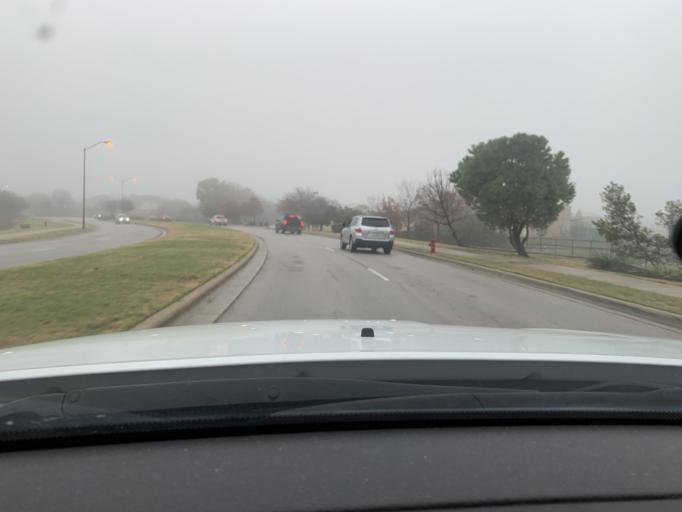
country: US
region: Texas
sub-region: Williamson County
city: Round Rock
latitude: 30.5645
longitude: -97.6820
